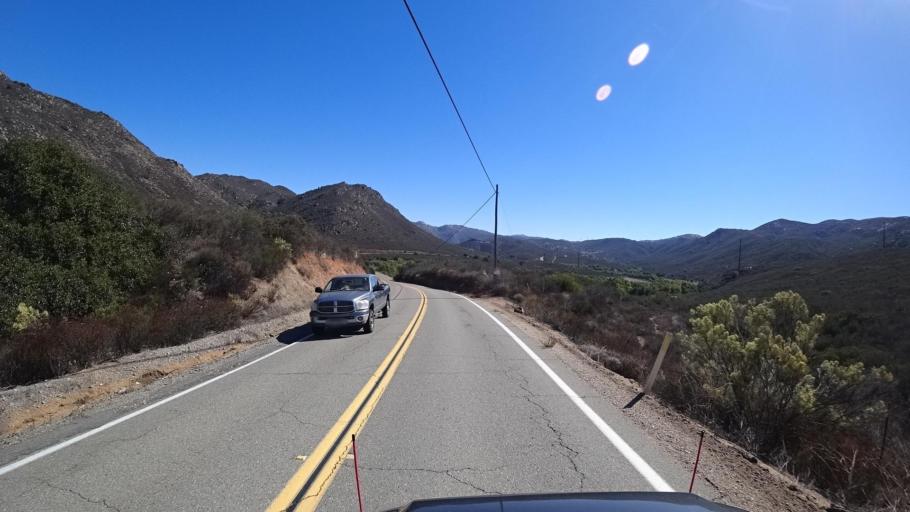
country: US
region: California
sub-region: San Diego County
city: Alpine
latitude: 32.7991
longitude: -116.7556
